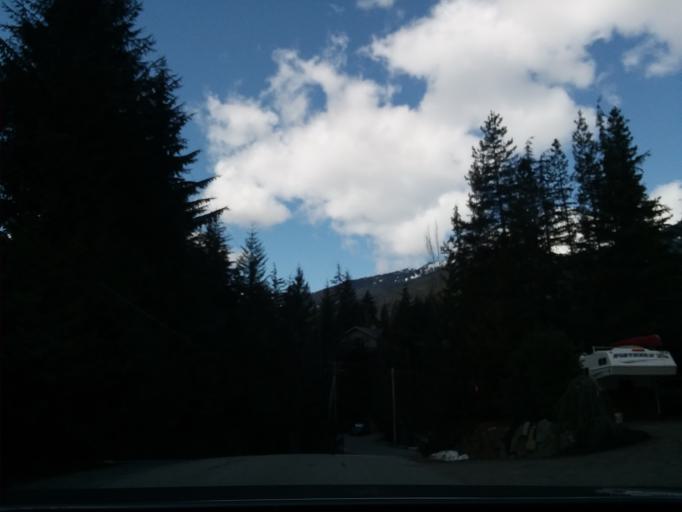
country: CA
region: British Columbia
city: Whistler
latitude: 50.0881
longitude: -122.9997
